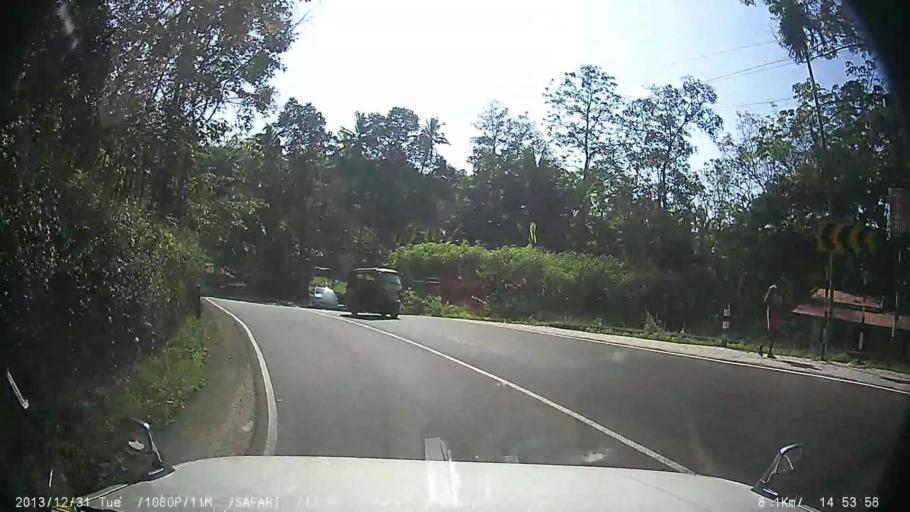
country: IN
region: Kerala
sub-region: Ernakulam
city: Piravam
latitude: 9.7690
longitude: 76.5106
